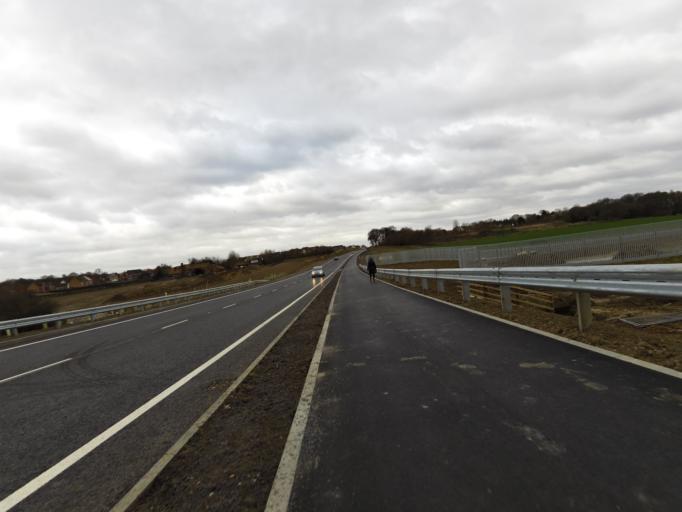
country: GB
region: England
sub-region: Norfolk
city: Hopton on Sea
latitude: 52.5053
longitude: 1.7293
